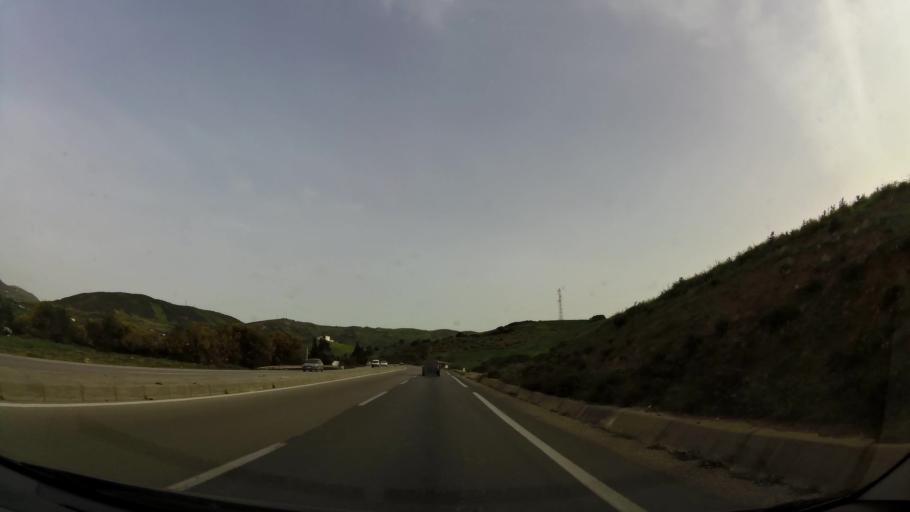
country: MA
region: Tanger-Tetouan
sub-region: Tanger-Assilah
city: Dar Chaoui
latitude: 35.5657
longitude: -5.6070
